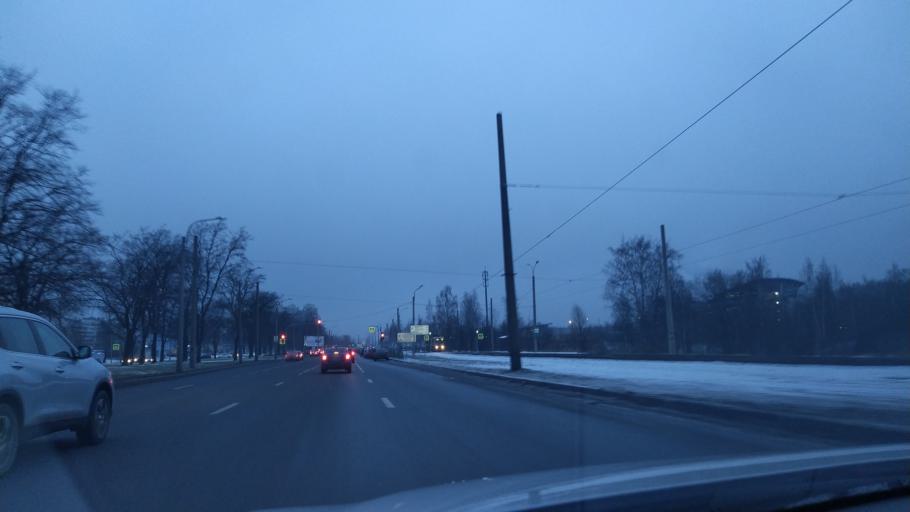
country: RU
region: St.-Petersburg
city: Grazhdanka
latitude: 60.0210
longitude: 30.4325
